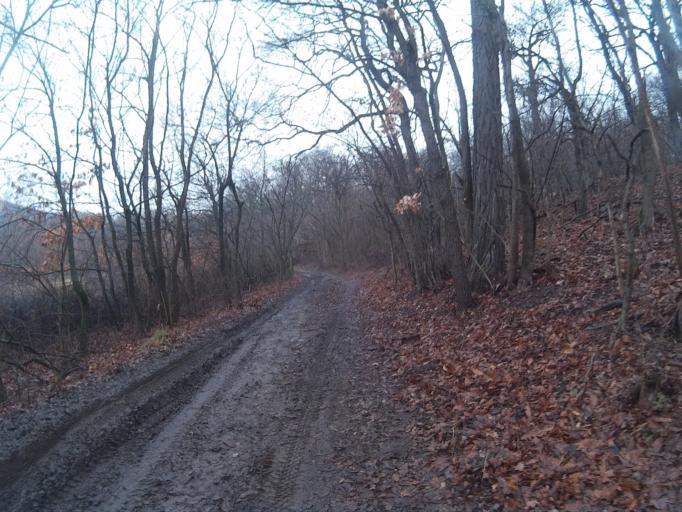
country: HU
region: Komarom-Esztergom
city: Nyergesujfalu
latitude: 47.7219
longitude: 18.5919
